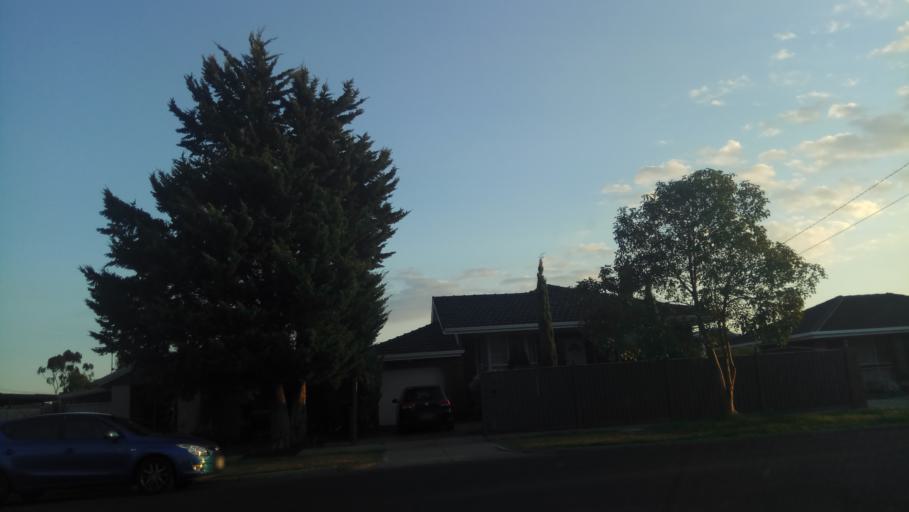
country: AU
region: Victoria
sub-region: Hobsons Bay
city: Altona Meadows
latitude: -37.8820
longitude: 144.7808
